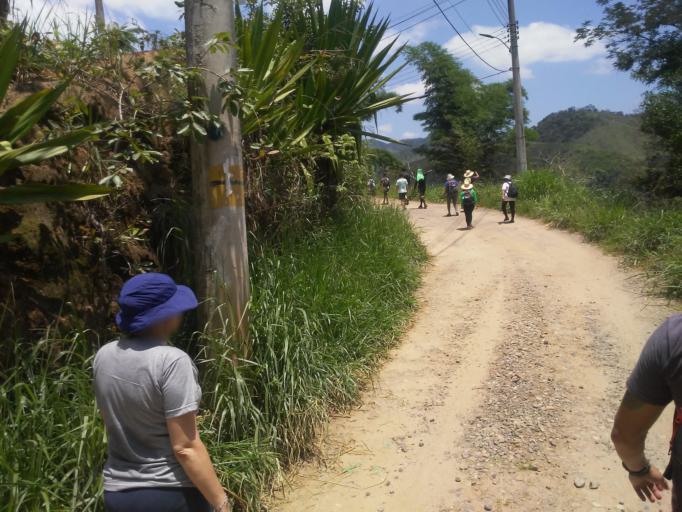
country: BR
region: Rio de Janeiro
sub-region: Paracambi
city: Paracambi
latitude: -22.6016
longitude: -43.6901
